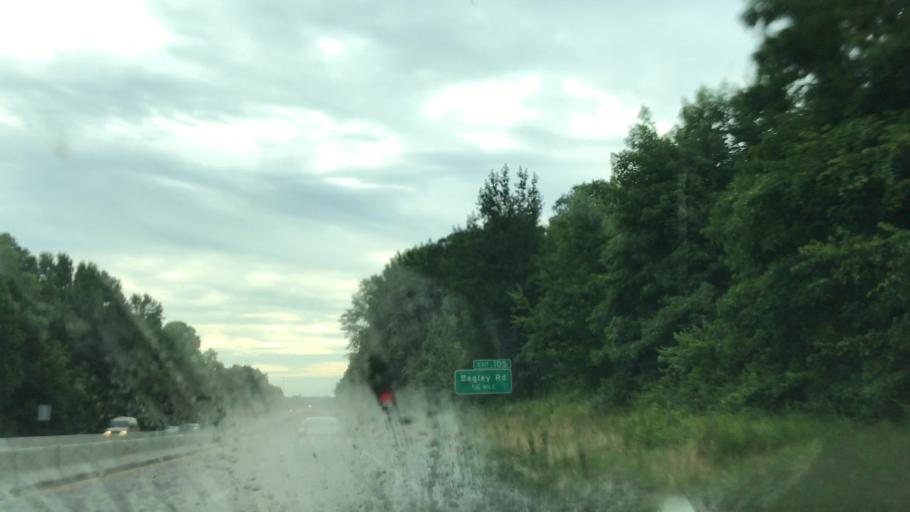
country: US
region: North Carolina
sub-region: Johnston County
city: Kenly
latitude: 35.5653
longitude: -78.1752
